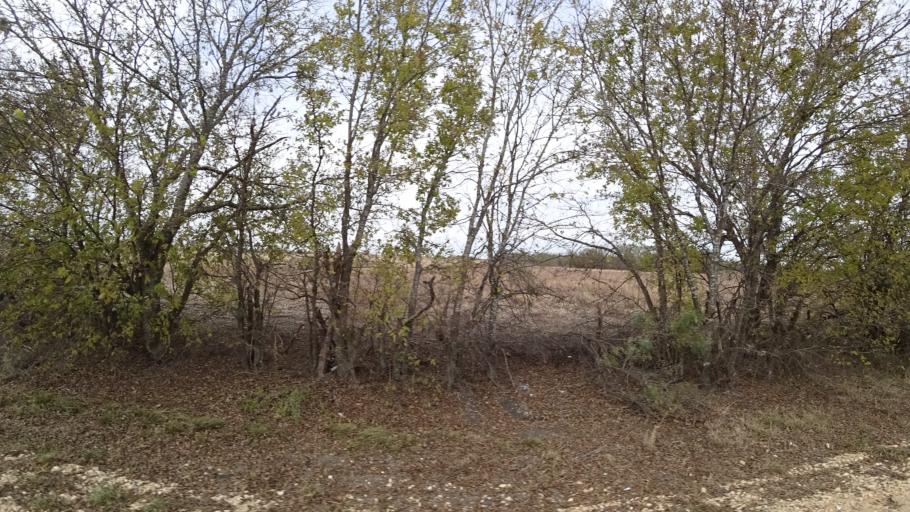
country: US
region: Texas
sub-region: Travis County
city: Garfield
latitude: 30.1470
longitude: -97.6442
